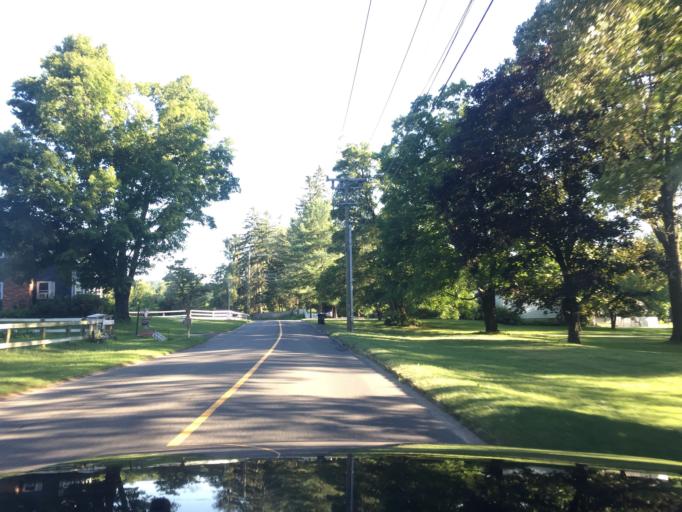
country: US
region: Connecticut
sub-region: Fairfield County
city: Bethel
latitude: 41.3892
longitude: -73.4004
